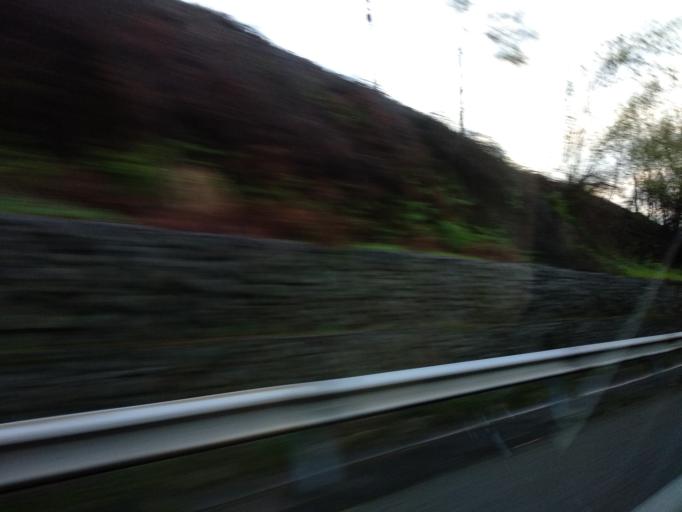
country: PT
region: Braga
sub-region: Braga
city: Oliveira
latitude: 41.4911
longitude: -8.4650
